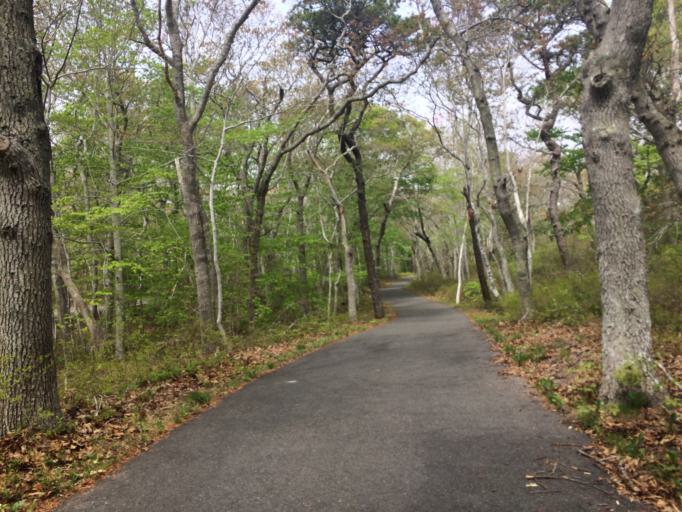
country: US
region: Massachusetts
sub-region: Barnstable County
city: Provincetown
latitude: 42.0710
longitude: -70.1979
